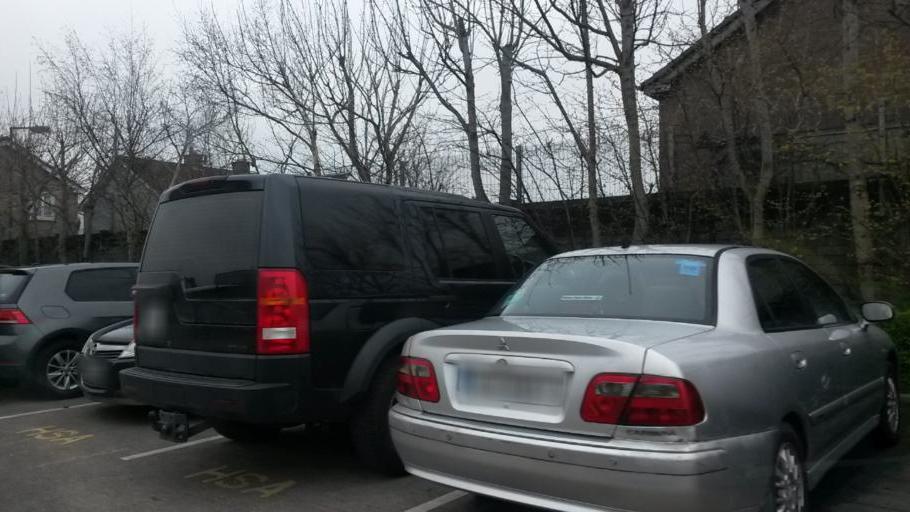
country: IE
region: Leinster
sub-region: Dublin City
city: Finglas
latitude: 53.3961
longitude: -6.3164
